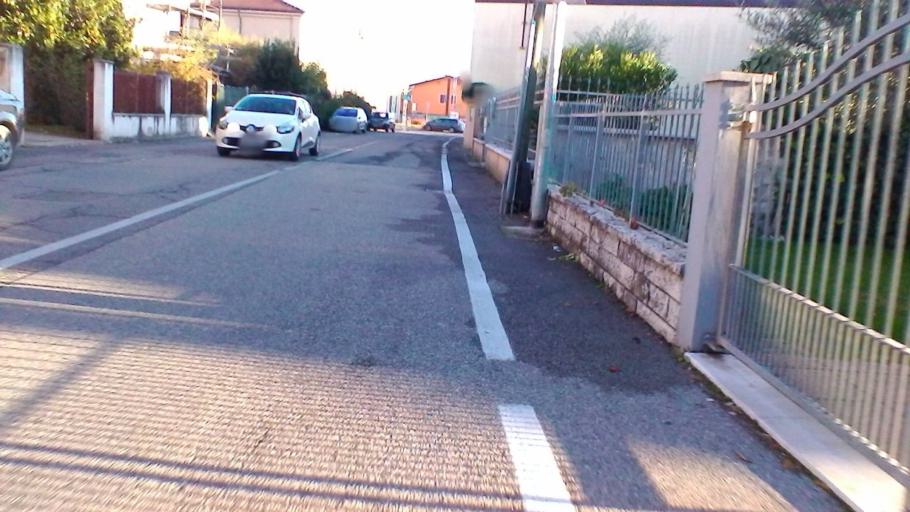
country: IT
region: Veneto
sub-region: Provincia di Verona
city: Povegliano Veronese
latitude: 45.3501
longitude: 10.8794
